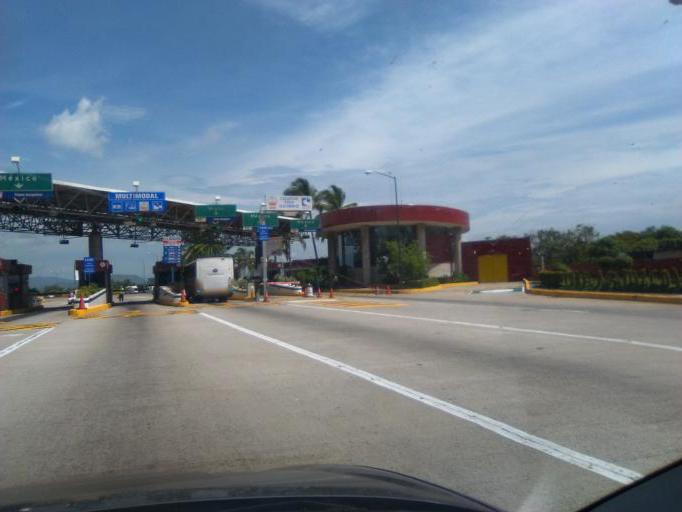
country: MX
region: Guerrero
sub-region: Acapulco de Juarez
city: Colonia Alborada
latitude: 16.8857
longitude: -99.8395
